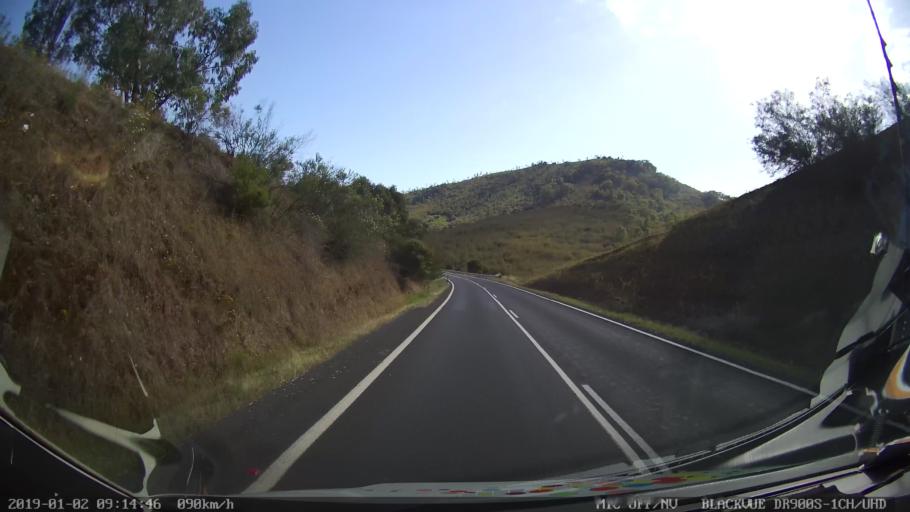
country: AU
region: New South Wales
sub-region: Tumut Shire
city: Tumut
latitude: -35.4731
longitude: 148.2772
